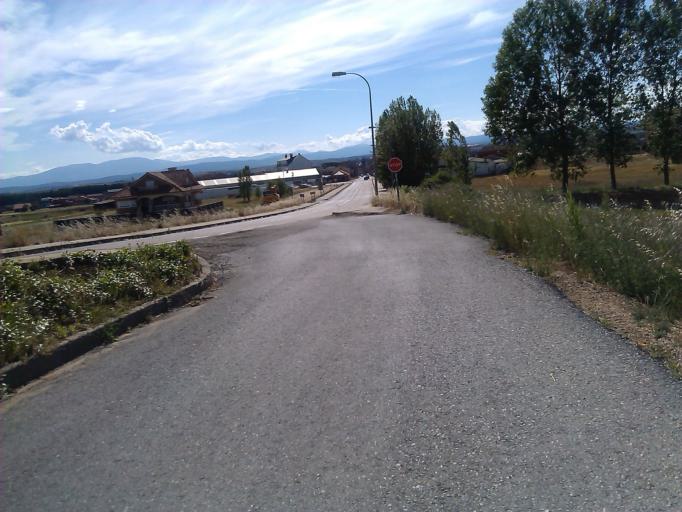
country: ES
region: Castille and Leon
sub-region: Provincia de Leon
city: San Justo de la Vega
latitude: 42.4544
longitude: -6.0072
